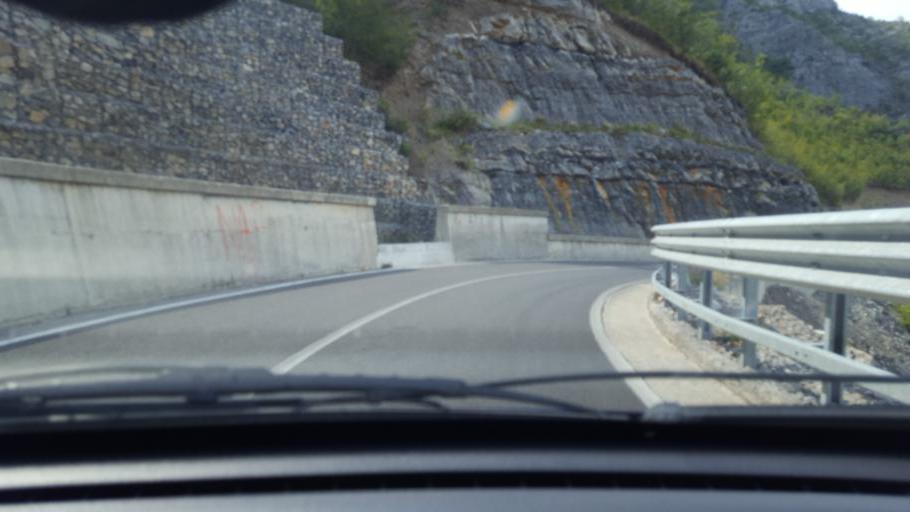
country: AL
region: Shkoder
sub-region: Rrethi i Malesia e Madhe
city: Kastrat
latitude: 42.4143
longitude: 19.4991
